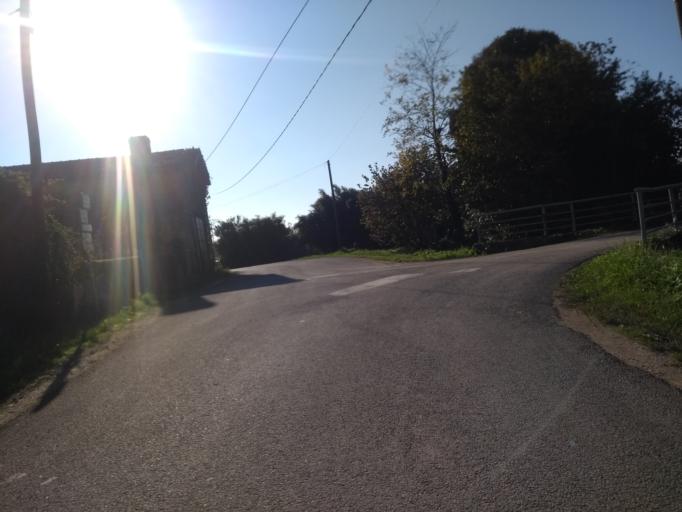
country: FR
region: Aquitaine
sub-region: Departement de la Gironde
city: Cambes
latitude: 44.7226
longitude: -0.4601
